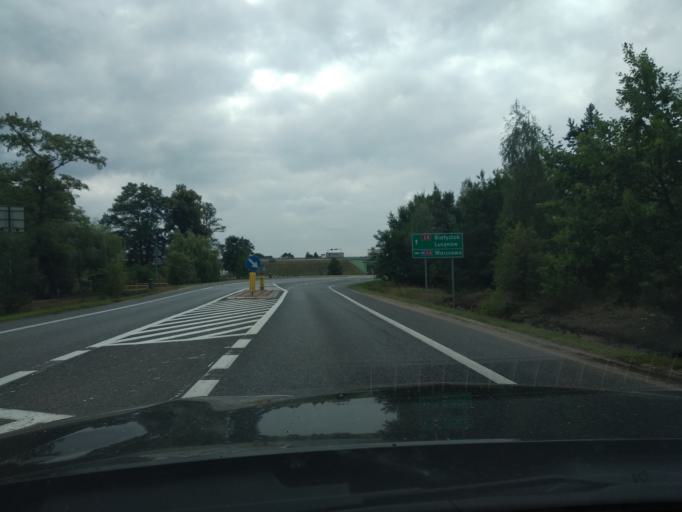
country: PL
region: Masovian Voivodeship
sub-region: Powiat wyszkowski
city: Wyszkow
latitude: 52.5599
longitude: 21.4621
